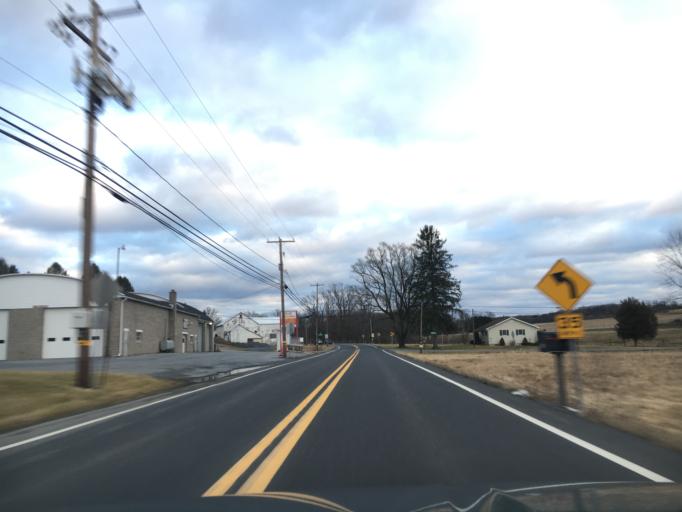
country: US
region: Pennsylvania
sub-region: Lehigh County
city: Schnecksville
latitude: 40.6854
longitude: -75.6849
